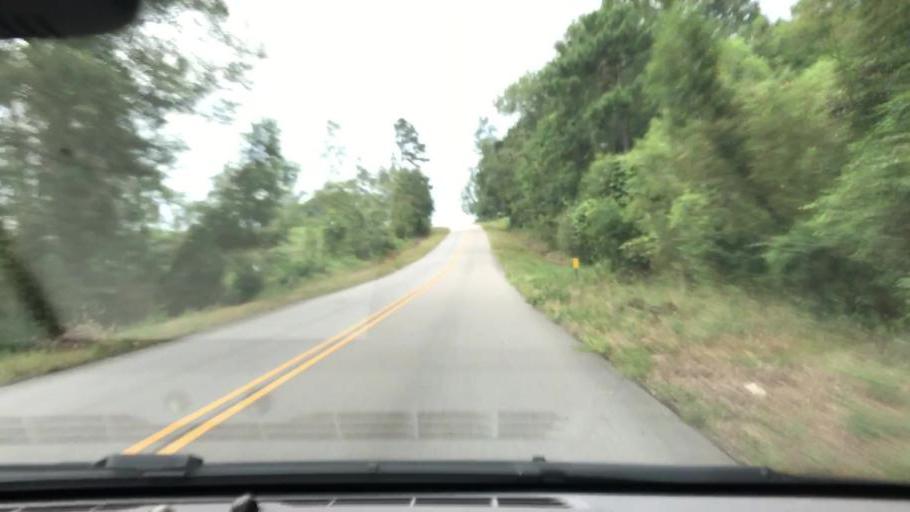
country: US
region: Alabama
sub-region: Houston County
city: Ashford
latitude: 31.2460
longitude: -85.1705
